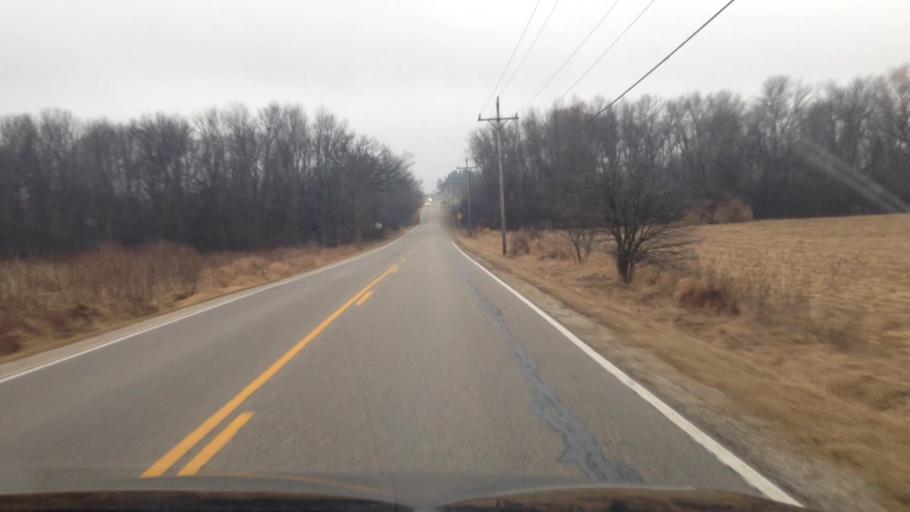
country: US
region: Wisconsin
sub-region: Washington County
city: Germantown
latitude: 43.2415
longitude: -88.1430
